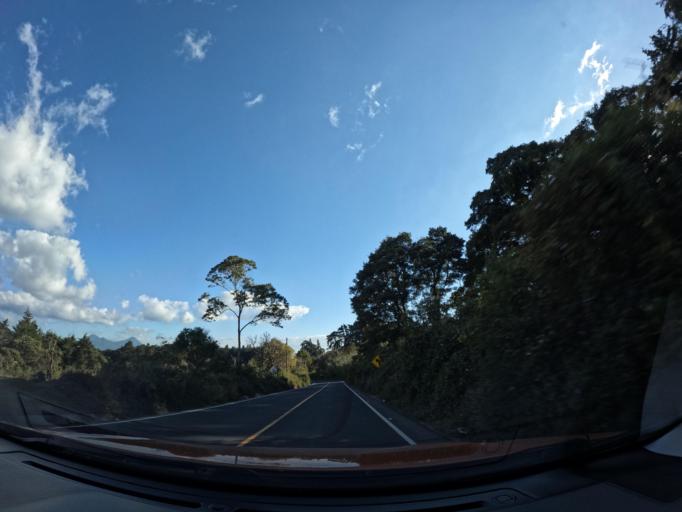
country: GT
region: Sacatepequez
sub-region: Municipio de Santa Maria de Jesus
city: Santa Maria de Jesus
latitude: 14.4796
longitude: -90.6999
